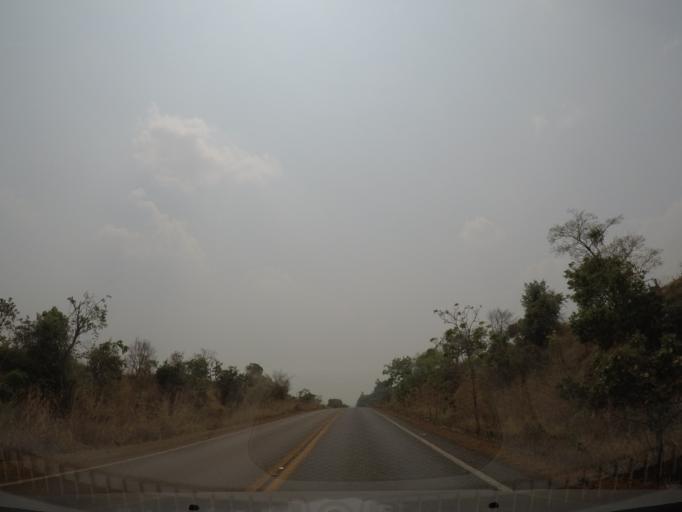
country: BR
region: Goias
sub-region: Pirenopolis
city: Pirenopolis
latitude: -15.9182
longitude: -48.8566
